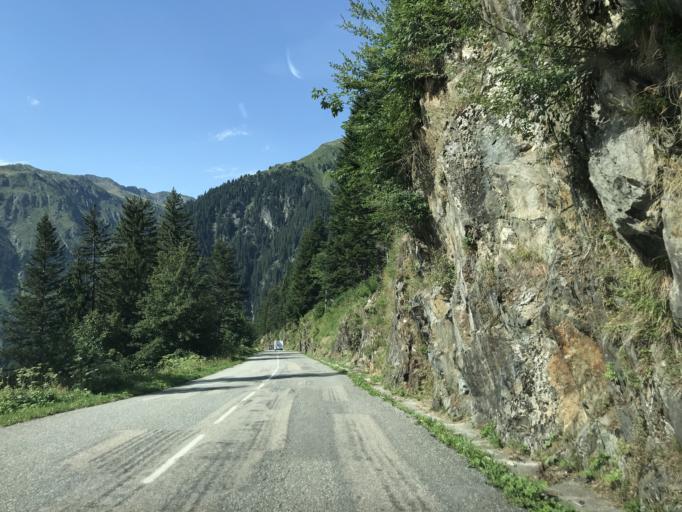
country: FR
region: Rhone-Alpes
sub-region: Departement de la Savoie
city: Beaufort
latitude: 45.7004
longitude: 6.6338
